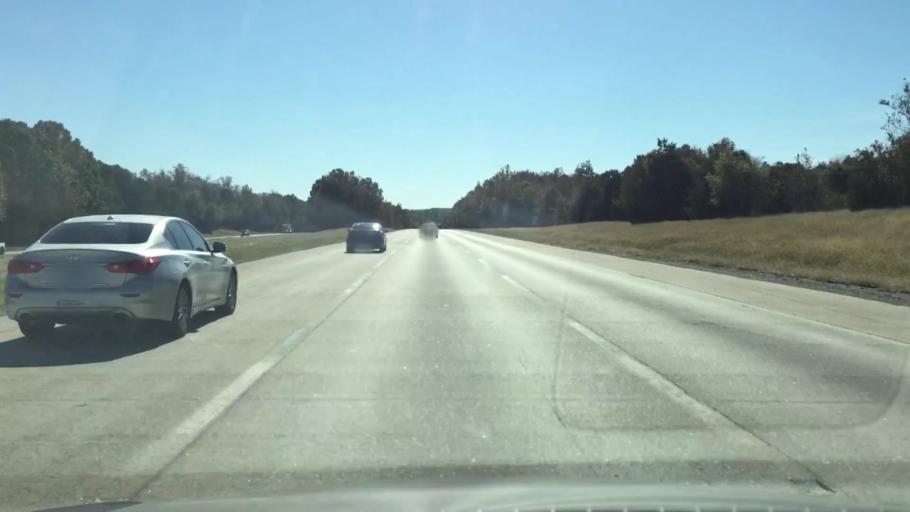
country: US
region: North Carolina
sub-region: Guilford County
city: Jamestown
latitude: 35.9566
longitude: -79.8969
